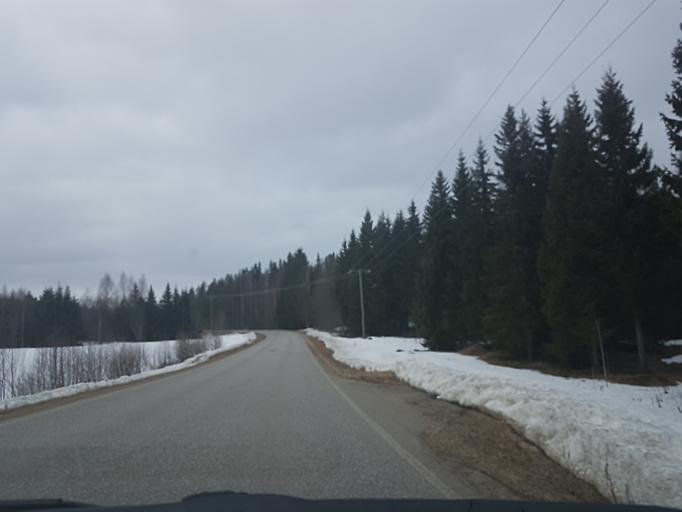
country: FI
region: Northern Savo
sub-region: Koillis-Savo
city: Kaavi
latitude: 63.0094
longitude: 28.6655
